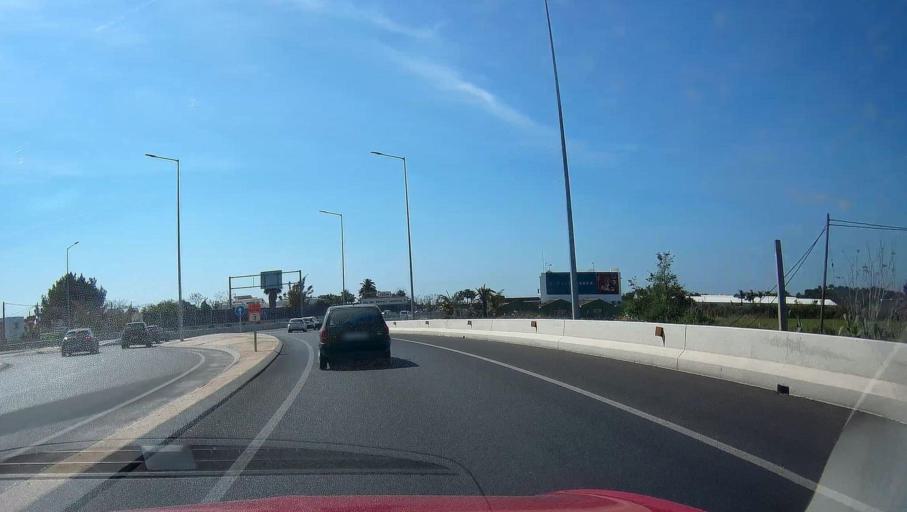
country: ES
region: Balearic Islands
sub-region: Illes Balears
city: Ibiza
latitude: 38.9355
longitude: 1.4437
